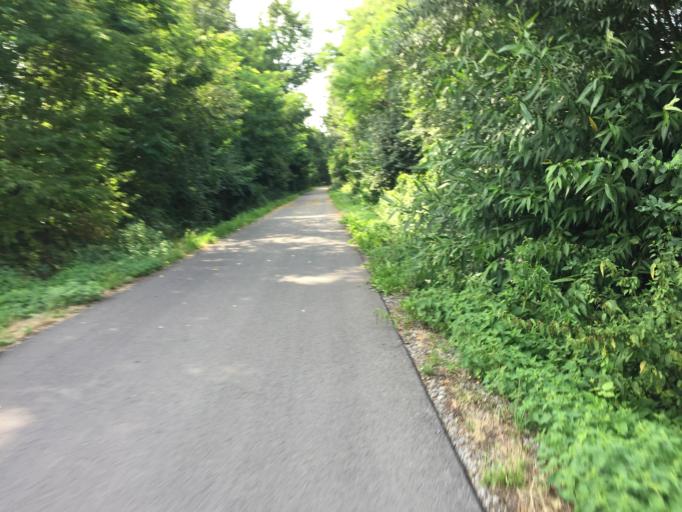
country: DE
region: Hesse
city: Schwalmstadt
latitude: 50.9079
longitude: 9.2106
